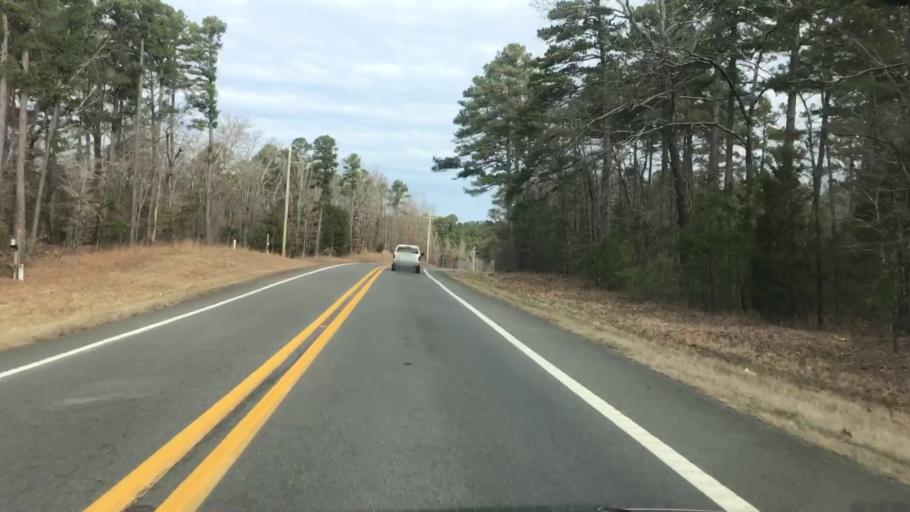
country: US
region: Arkansas
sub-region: Montgomery County
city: Mount Ida
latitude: 34.5884
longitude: -93.6637
